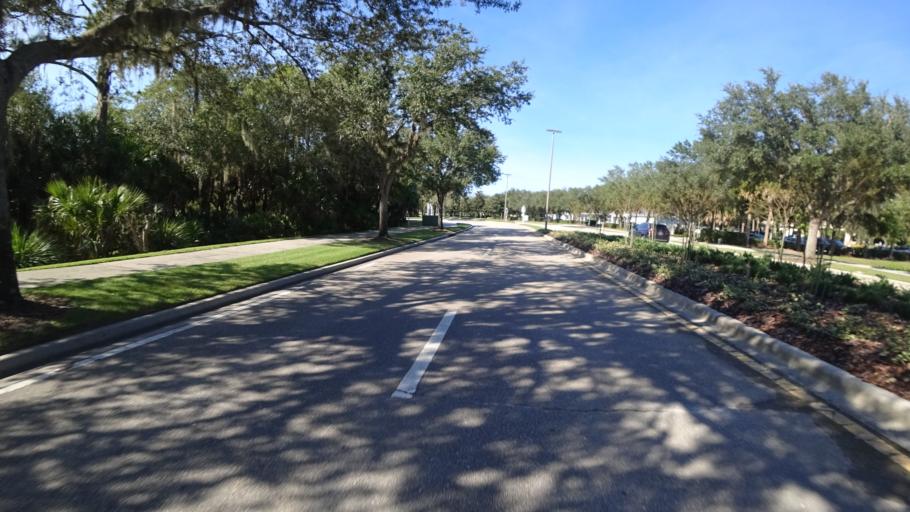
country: US
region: Florida
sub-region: Sarasota County
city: The Meadows
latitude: 27.3932
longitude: -82.4461
